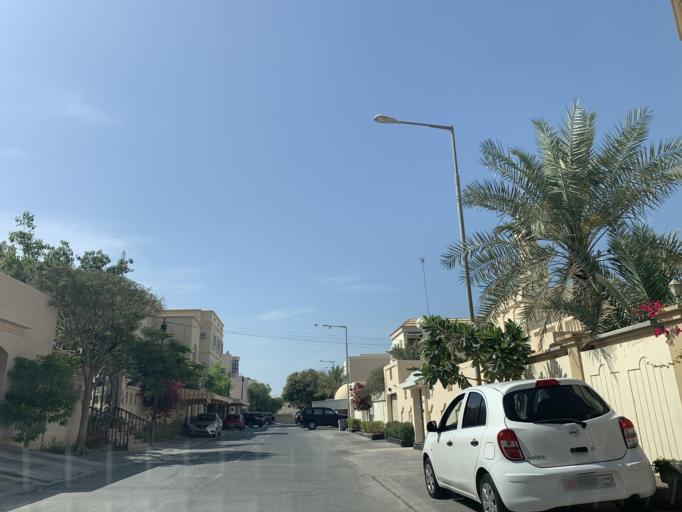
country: BH
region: Northern
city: Ar Rifa'
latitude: 26.1299
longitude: 50.5823
